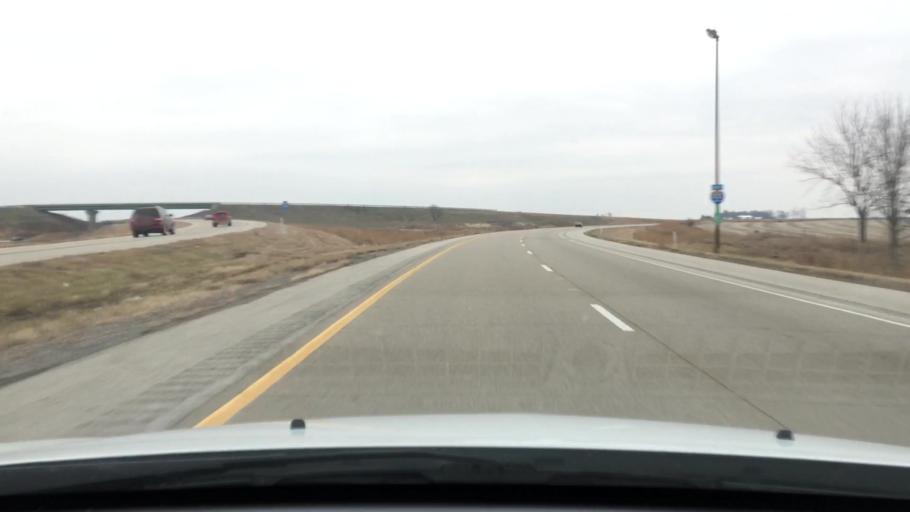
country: US
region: Illinois
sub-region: Logan County
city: Lincoln
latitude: 40.1747
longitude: -89.4160
